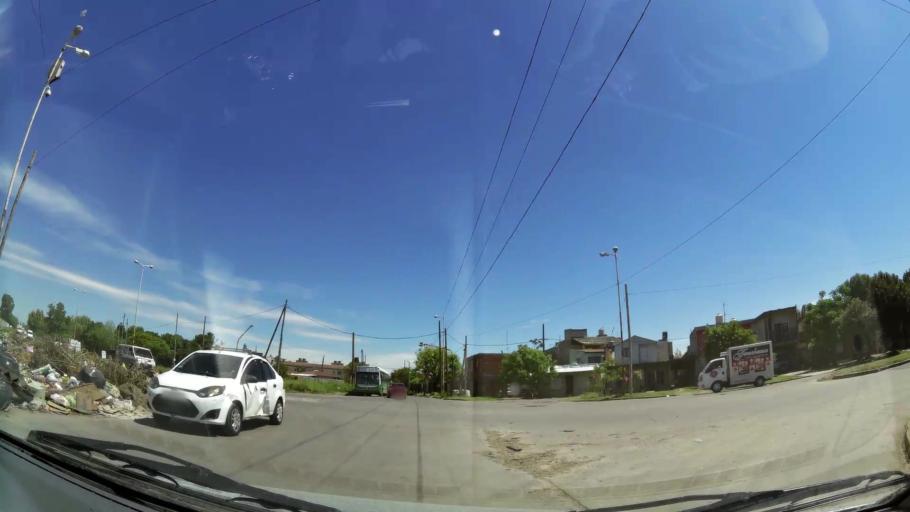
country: AR
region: Buenos Aires
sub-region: Partido de Lanus
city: Lanus
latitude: -34.7365
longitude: -58.3440
